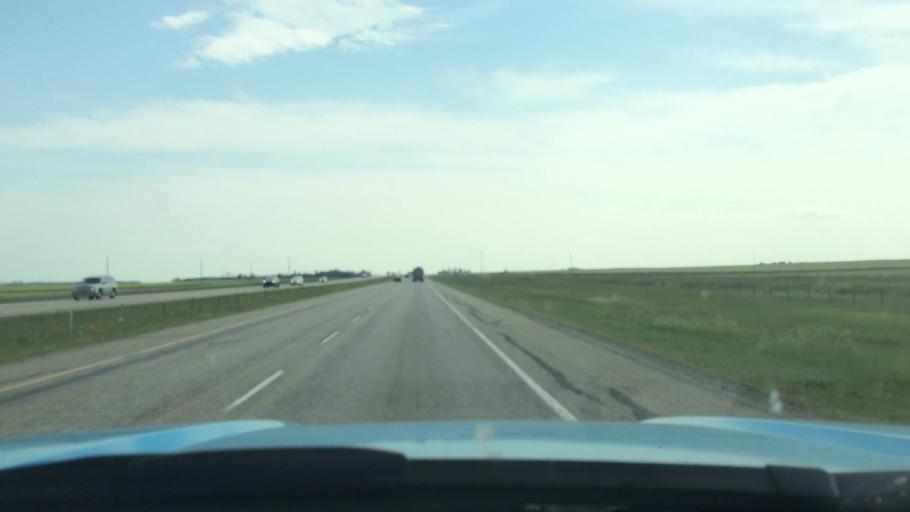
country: CA
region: Alberta
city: Olds
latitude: 51.8273
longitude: -114.0254
